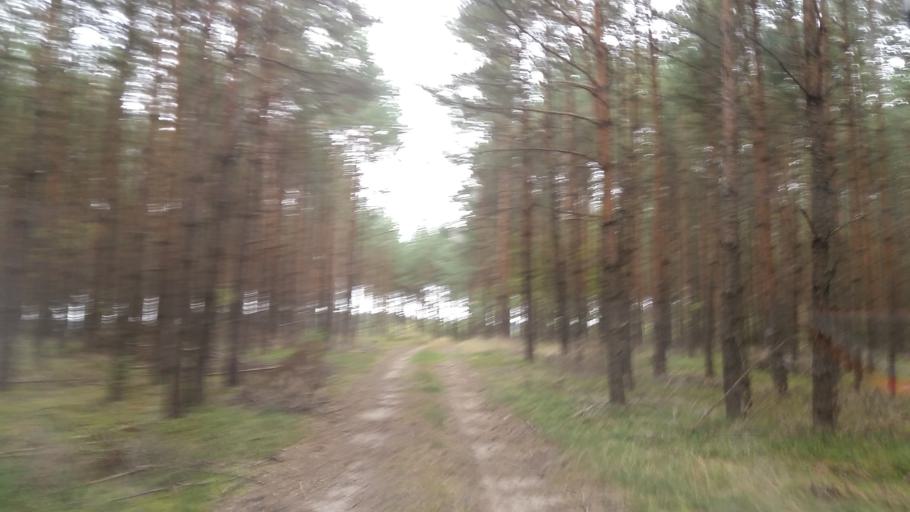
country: PL
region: West Pomeranian Voivodeship
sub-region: Powiat choszczenski
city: Bierzwnik
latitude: 52.9860
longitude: 15.6006
